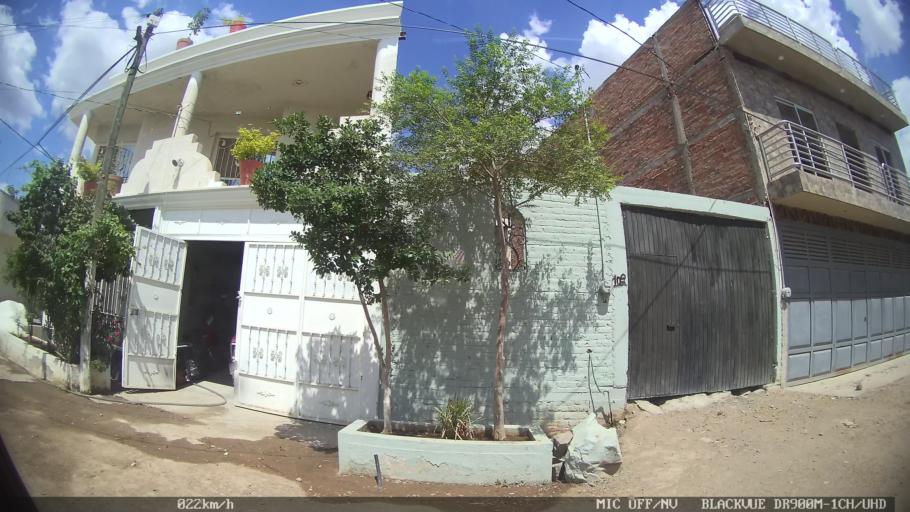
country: MX
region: Jalisco
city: Tlaquepaque
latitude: 20.6670
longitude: -103.2562
